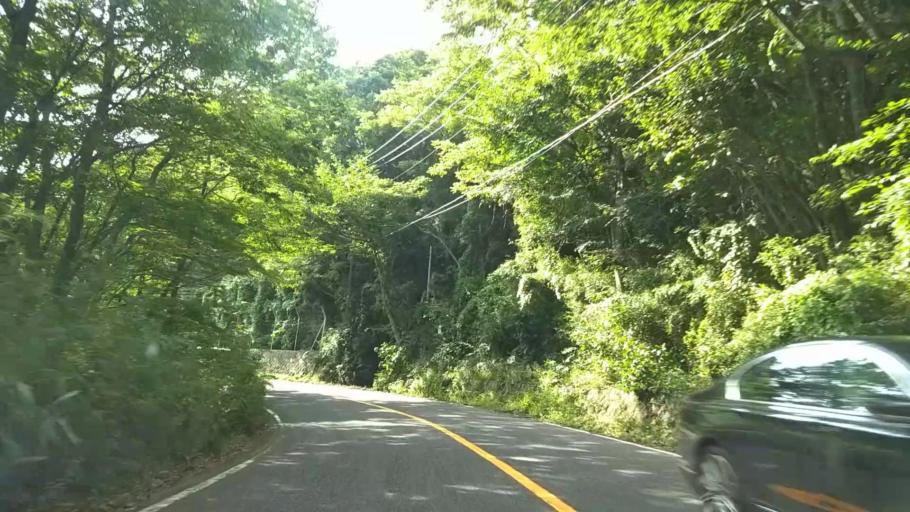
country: JP
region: Kanagawa
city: Hakone
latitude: 35.2638
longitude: 139.0249
